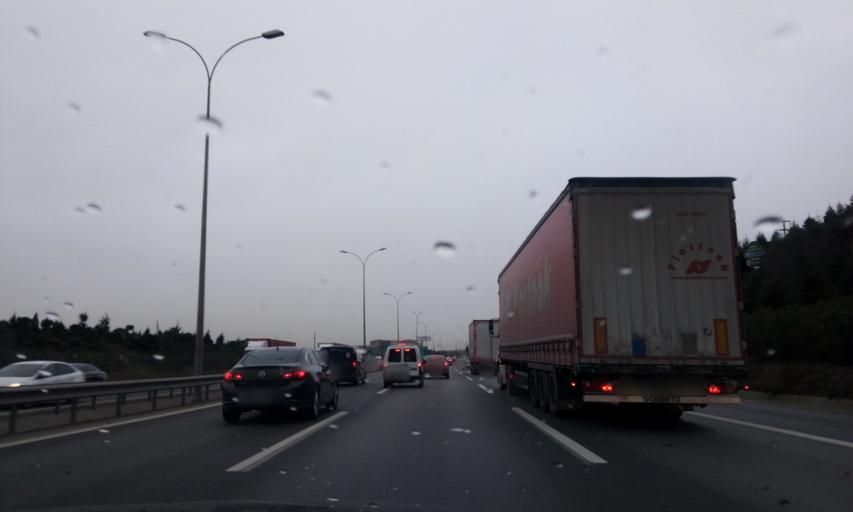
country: TR
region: Kocaeli
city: Balcik
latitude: 40.8616
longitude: 29.4026
